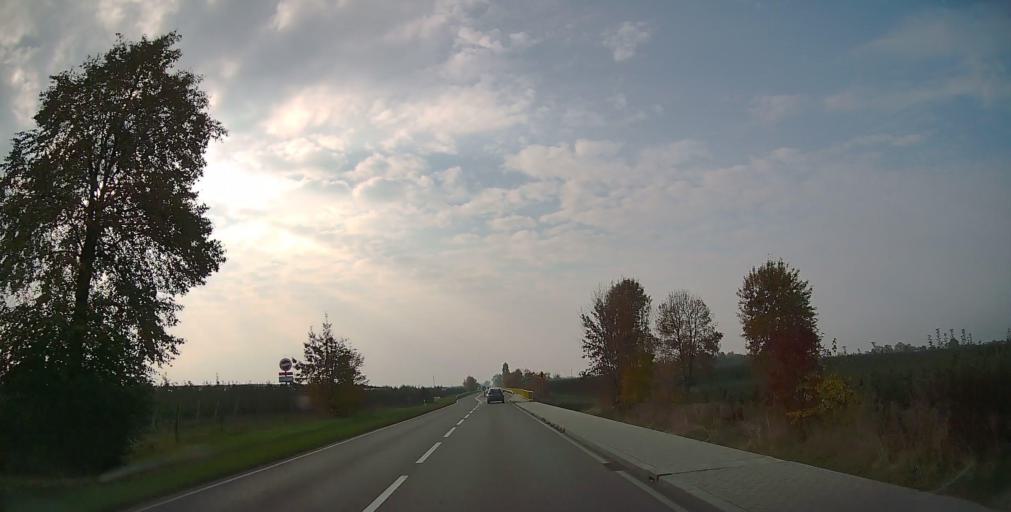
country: PL
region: Masovian Voivodeship
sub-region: Powiat grojecki
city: Belsk Duzy
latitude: 51.7681
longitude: 20.7683
